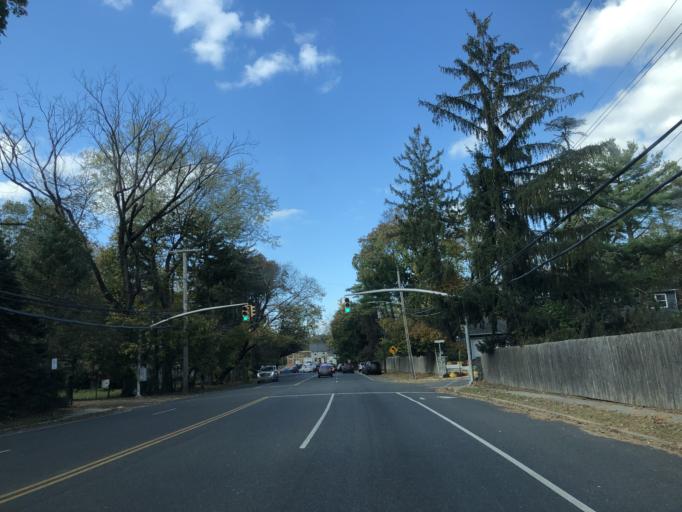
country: US
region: New York
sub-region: Nassau County
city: Roslyn Estates
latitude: 40.7981
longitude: -73.6572
